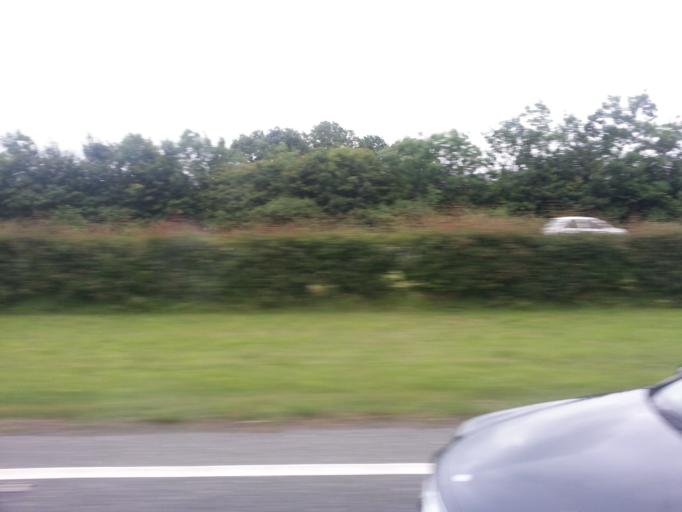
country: IE
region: Leinster
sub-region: Kildare
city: Kilcullen
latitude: 53.1902
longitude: -6.7283
